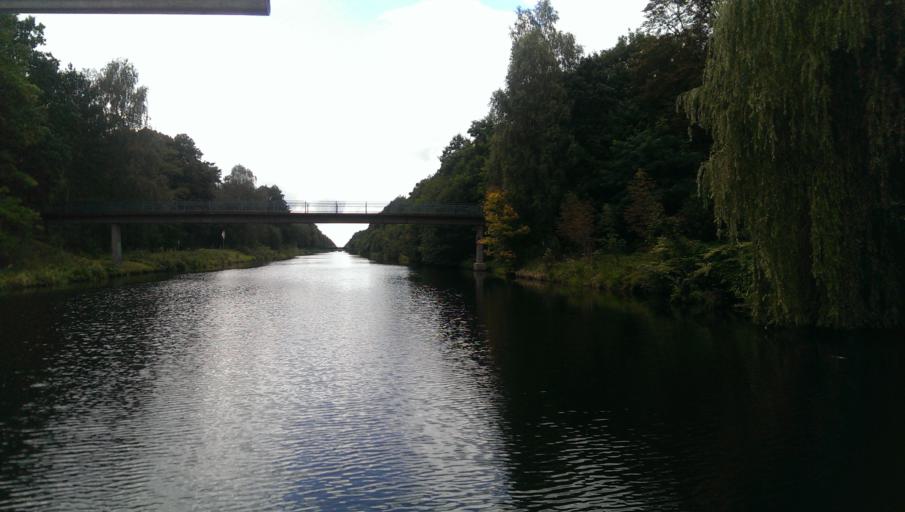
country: DE
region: Brandenburg
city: Marienwerder
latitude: 52.8463
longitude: 13.5378
